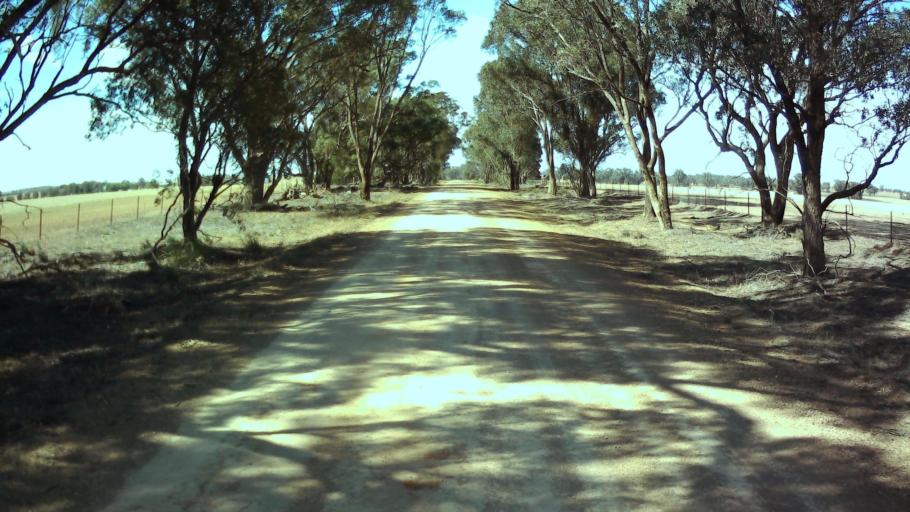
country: AU
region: New South Wales
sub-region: Weddin
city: Grenfell
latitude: -34.0547
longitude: 148.3132
